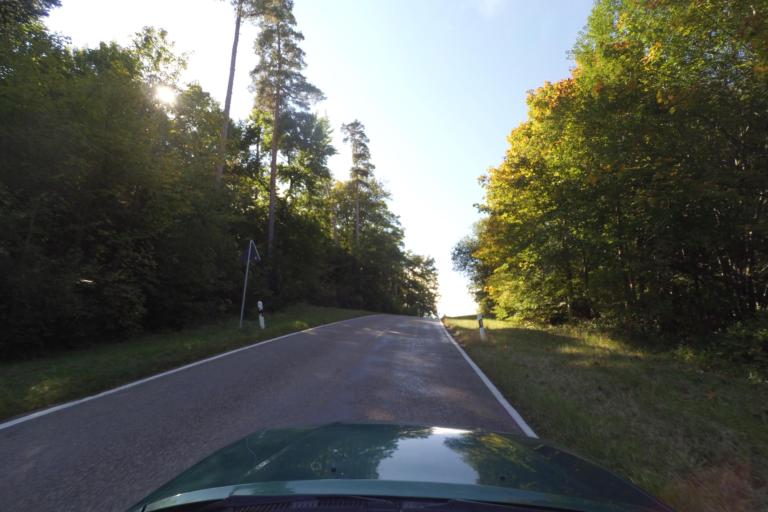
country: DE
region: Baden-Wuerttemberg
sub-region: Karlsruhe Region
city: Simmozheim
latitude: 48.7728
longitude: 8.8018
